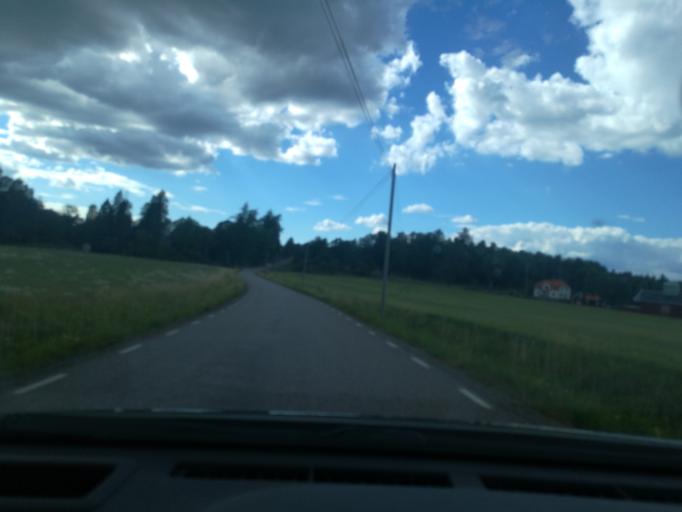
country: SE
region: Soedermanland
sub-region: Eskilstuna Kommun
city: Arla
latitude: 59.4416
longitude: 16.7905
